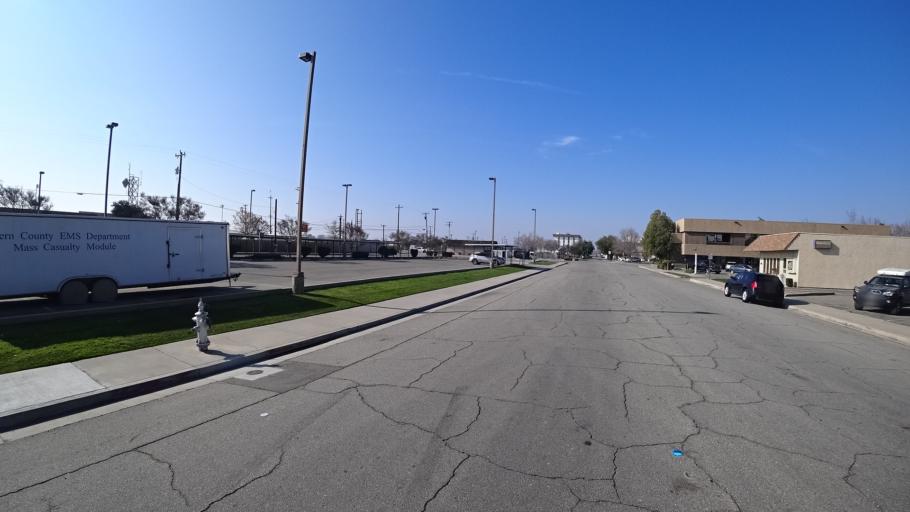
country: US
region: California
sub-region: Kern County
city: Bakersfield
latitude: 35.3723
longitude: -119.0248
